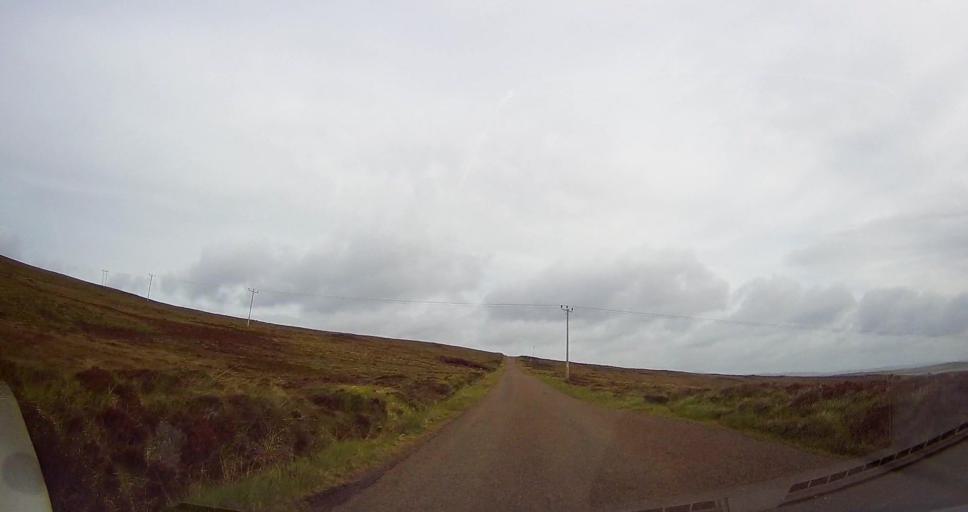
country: GB
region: Scotland
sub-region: Orkney Islands
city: Stromness
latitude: 58.8622
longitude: -3.2227
